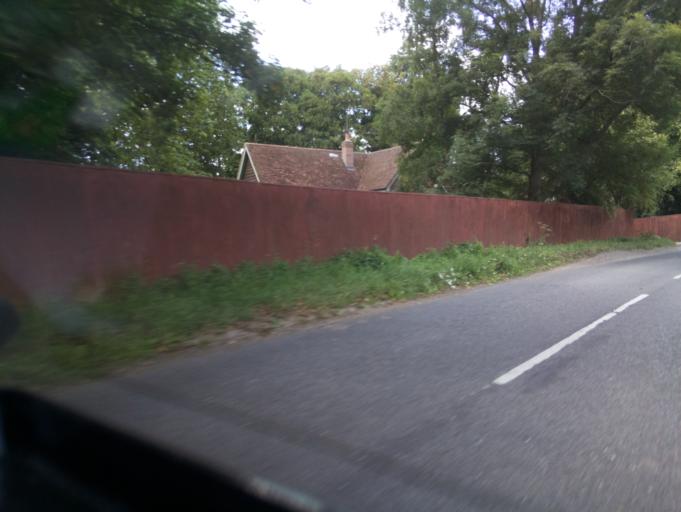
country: GB
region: England
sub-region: Oxfordshire
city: Faringdon
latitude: 51.6301
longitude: -1.5859
